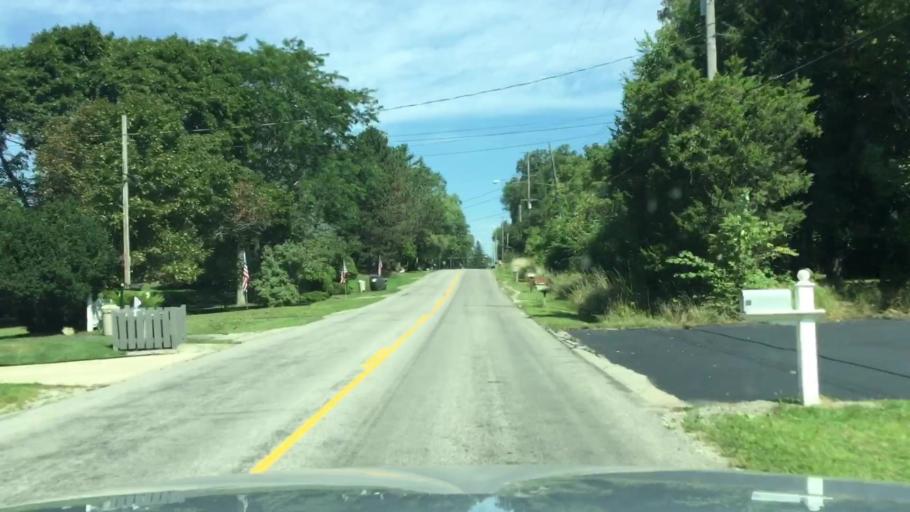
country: US
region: Michigan
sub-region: Lenawee County
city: Manitou Beach-Devils Lake
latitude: 41.9994
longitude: -84.2808
